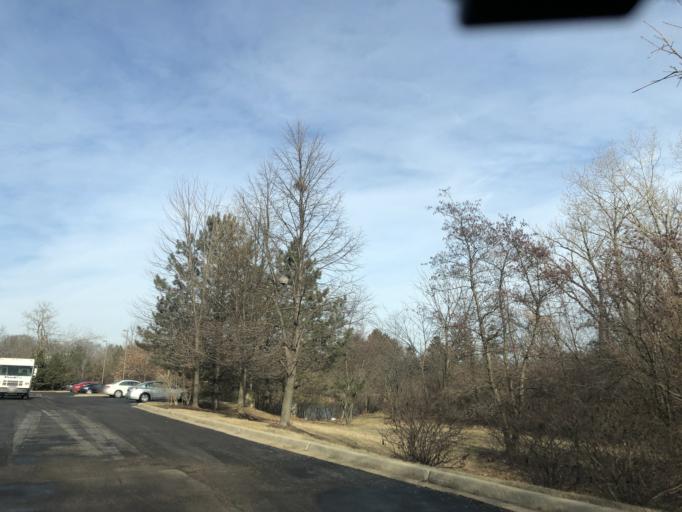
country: US
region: Illinois
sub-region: Cook County
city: Lemont
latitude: 41.7202
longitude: -88.0096
